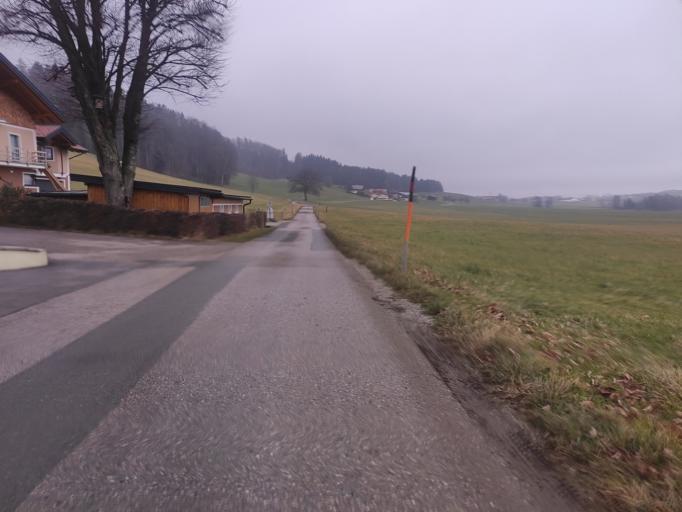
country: AT
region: Salzburg
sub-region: Politischer Bezirk Salzburg-Umgebung
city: Mattsee
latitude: 47.9560
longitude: 13.1224
